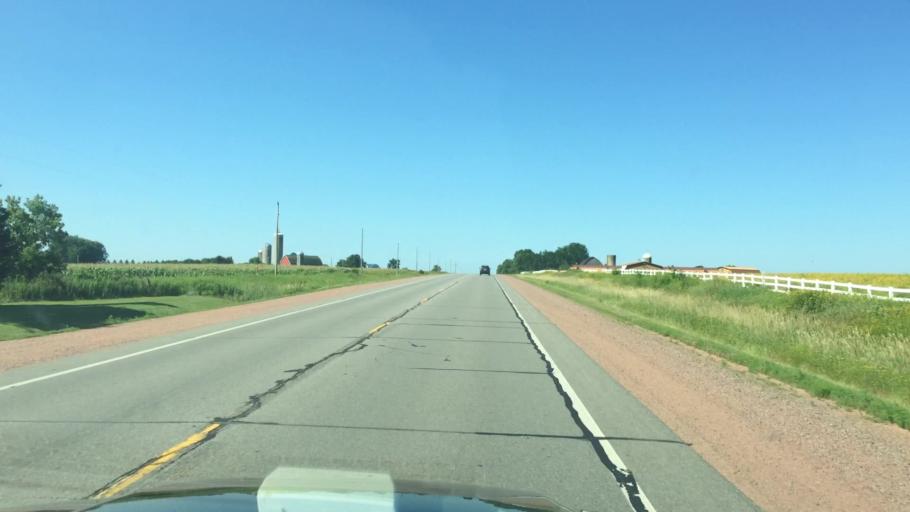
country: US
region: Wisconsin
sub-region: Marathon County
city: Stratford
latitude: 44.7325
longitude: -90.0839
